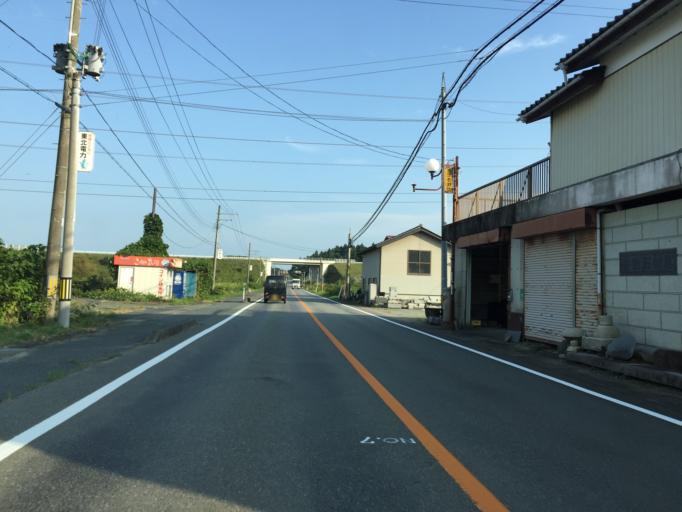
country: JP
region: Fukushima
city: Namie
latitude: 37.5061
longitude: 140.9396
